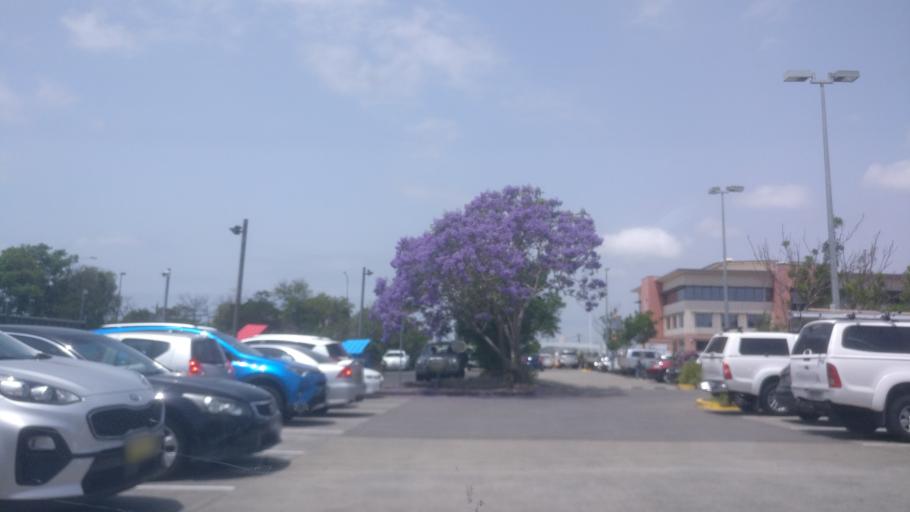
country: AU
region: New South Wales
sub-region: Shoalhaven Shire
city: Nowra
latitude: -34.8732
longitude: 150.6037
